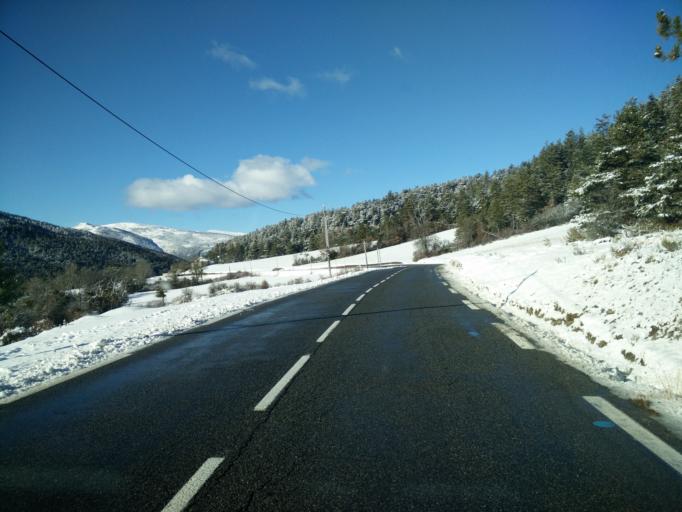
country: FR
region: Provence-Alpes-Cote d'Azur
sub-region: Departement des Alpes-de-Haute-Provence
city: Annot
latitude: 43.9126
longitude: 6.6005
